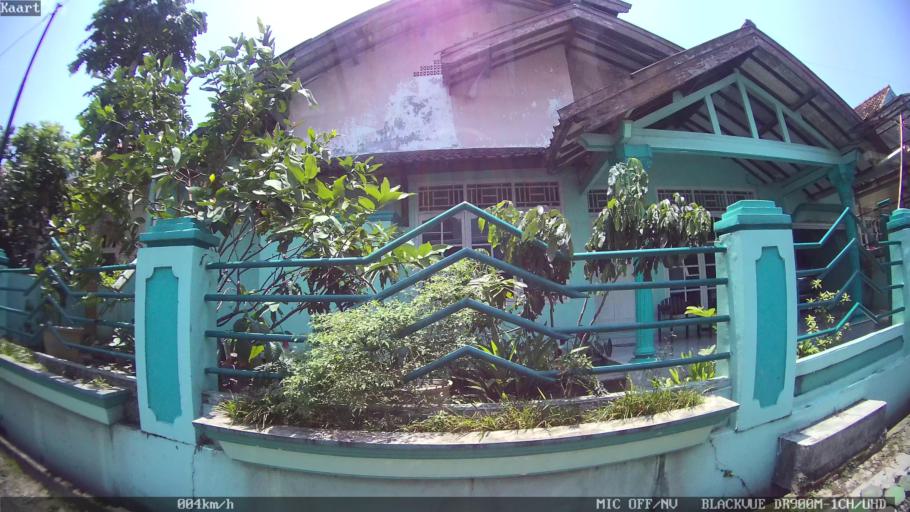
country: ID
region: Lampung
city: Kedaton
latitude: -5.3953
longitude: 105.2909
